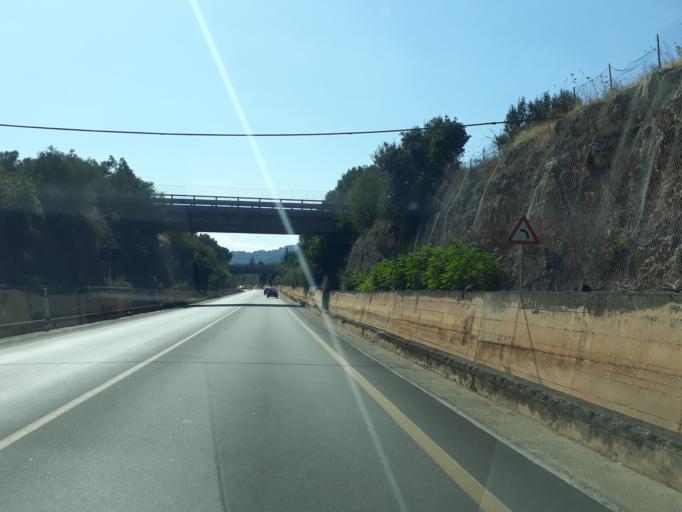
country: IT
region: Apulia
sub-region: Provincia di Brindisi
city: Fasano
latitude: 40.8396
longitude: 17.3518
